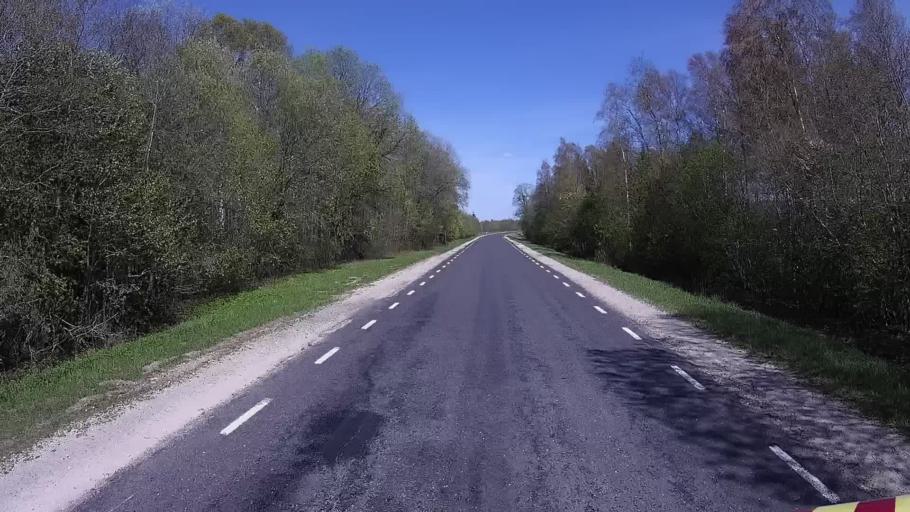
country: EE
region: Laeaene
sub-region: Ridala Parish
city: Uuemoisa
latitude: 59.0100
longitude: 23.7830
